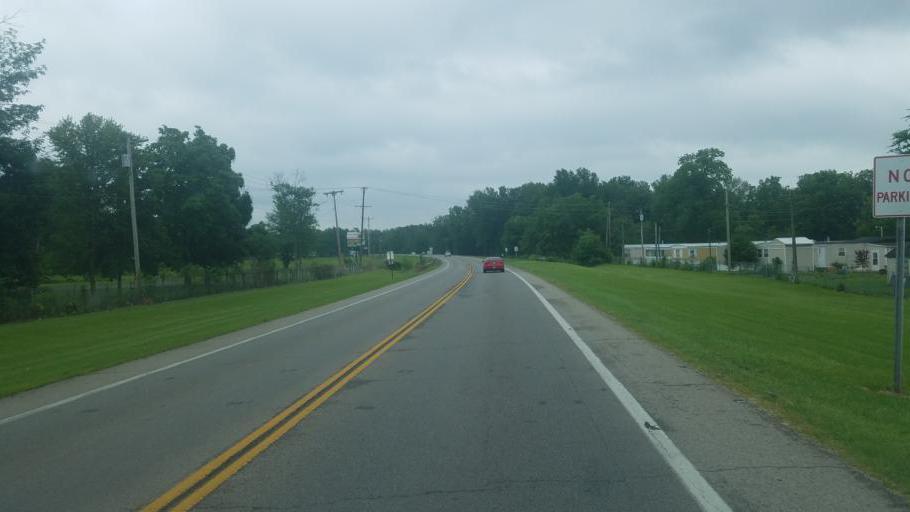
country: US
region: Ohio
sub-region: Logan County
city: Lakeview
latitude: 40.4827
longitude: -83.9199
